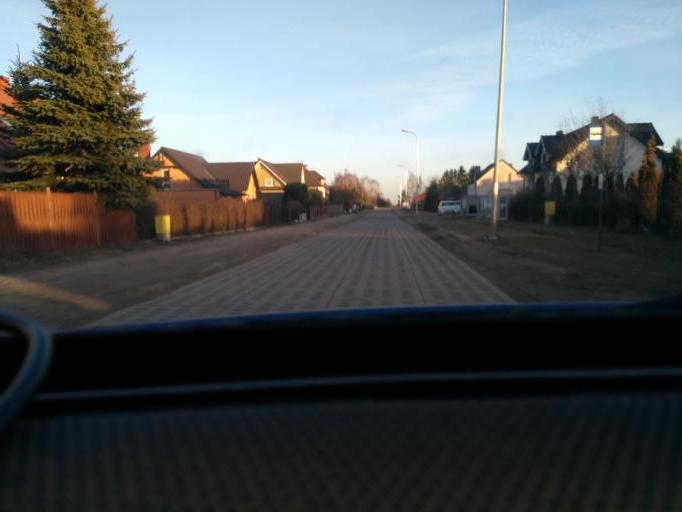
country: PL
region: Pomeranian Voivodeship
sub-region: Powiat kartuski
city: Banino
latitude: 54.3846
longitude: 18.3897
